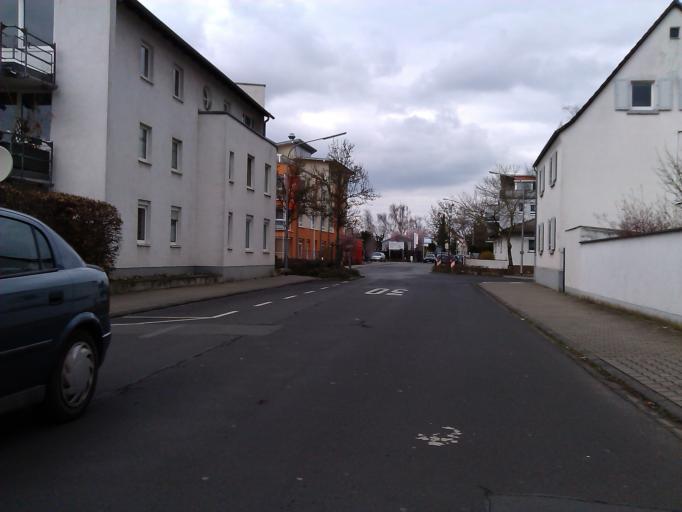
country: DE
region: Hesse
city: Griesheim
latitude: 49.8657
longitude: 8.5560
